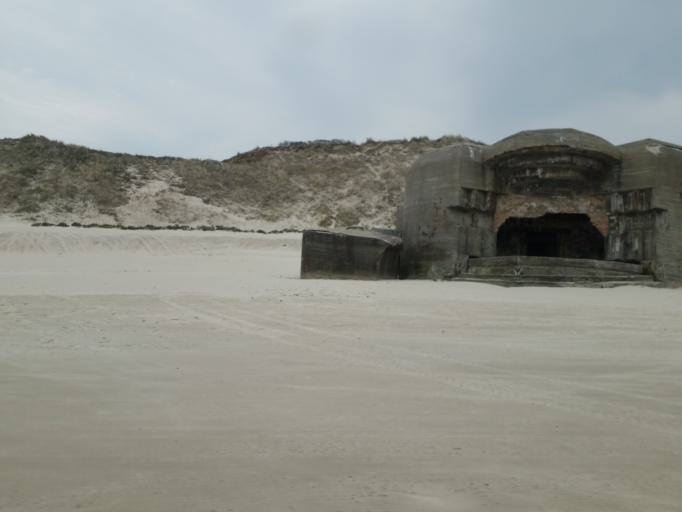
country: DK
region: North Denmark
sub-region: Jammerbugt Kommune
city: Pandrup
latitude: 57.3808
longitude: 9.7175
